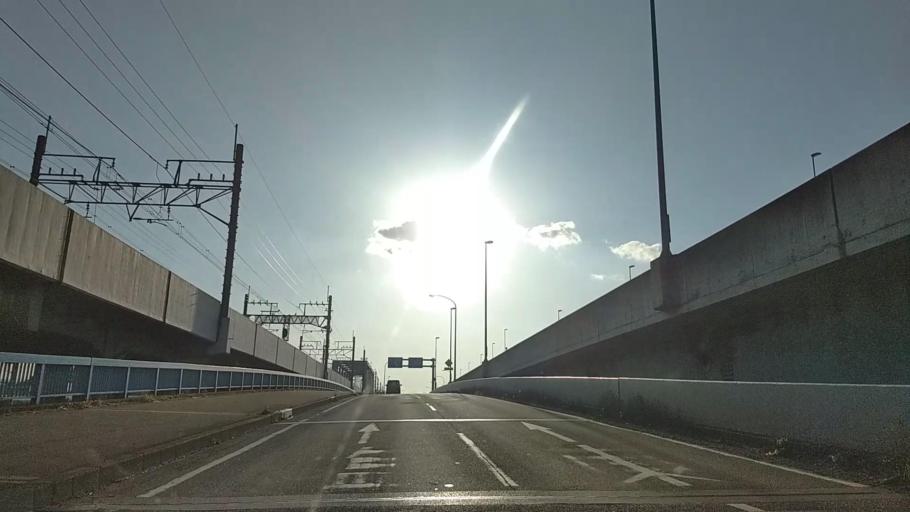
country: JP
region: Tokyo
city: Urayasu
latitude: 35.6769
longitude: 139.9331
